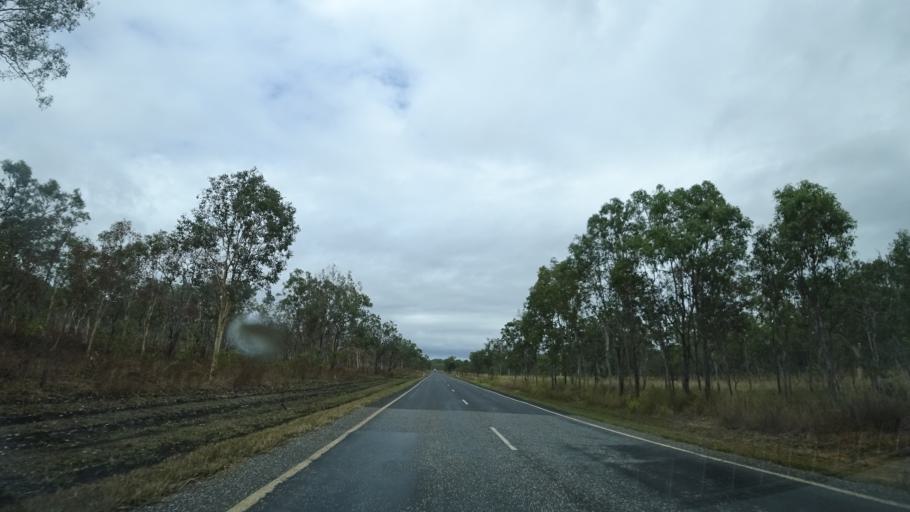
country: AU
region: Queensland
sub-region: Tablelands
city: Mareeba
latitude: -16.7644
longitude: 145.3413
